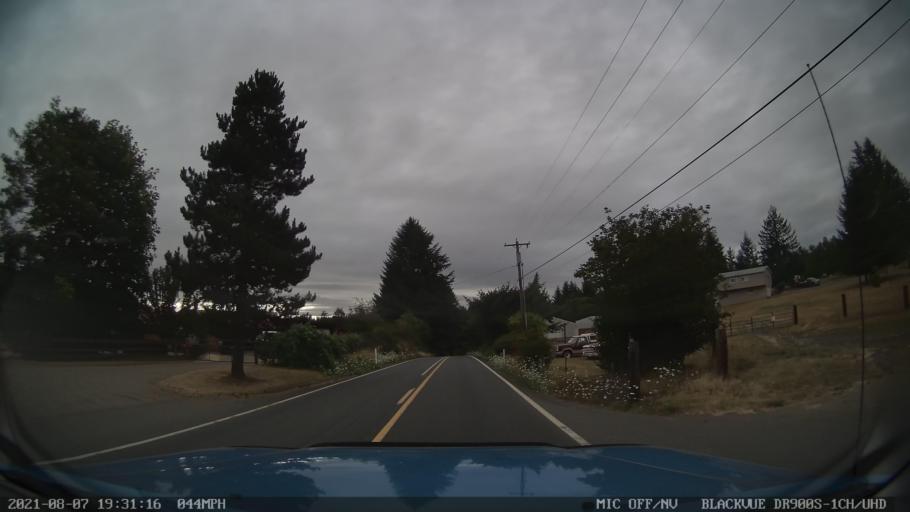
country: US
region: Oregon
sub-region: Linn County
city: Lyons
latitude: 44.8904
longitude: -122.6314
